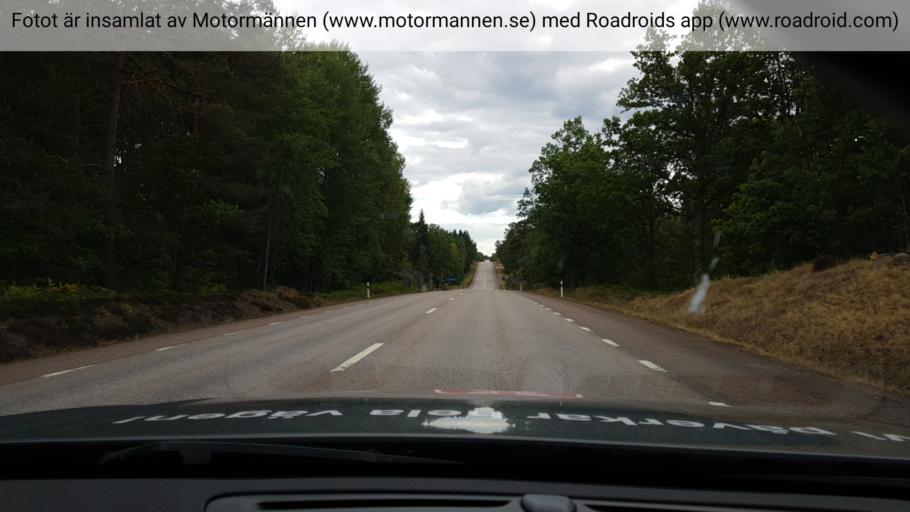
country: SE
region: Kalmar
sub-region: Oskarshamns Kommun
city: Oskarshamn
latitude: 57.4795
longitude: 16.5177
